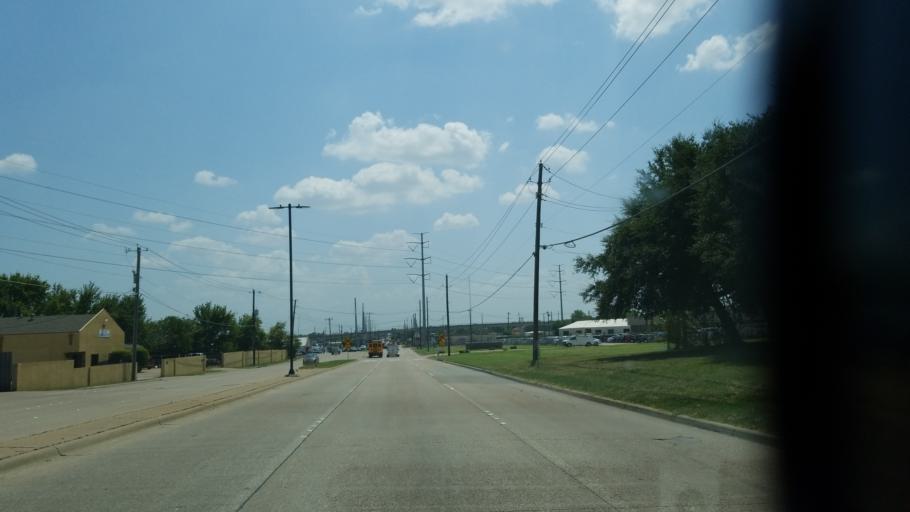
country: US
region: Texas
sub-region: Dallas County
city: Garland
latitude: 32.9212
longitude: -96.6308
